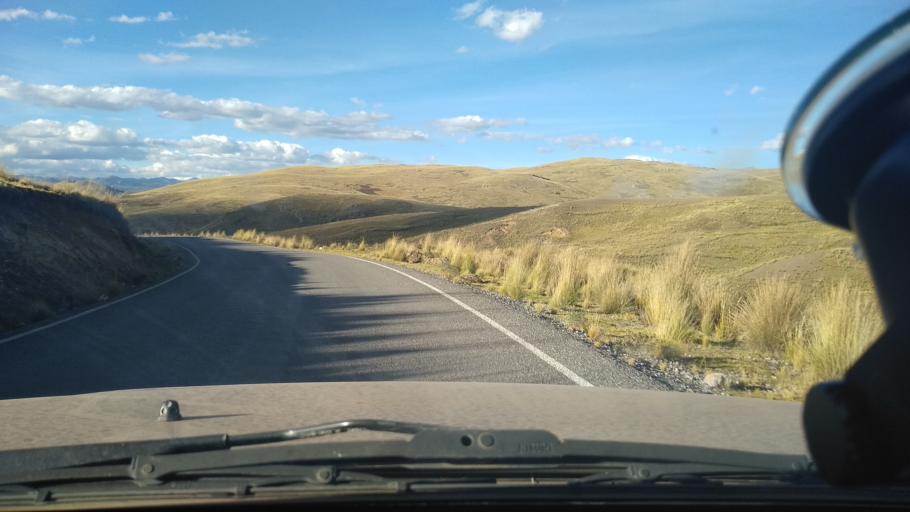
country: PE
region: Cusco
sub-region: Provincia de Canas
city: Ccaquiracunca
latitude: -14.2824
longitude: -71.4494
